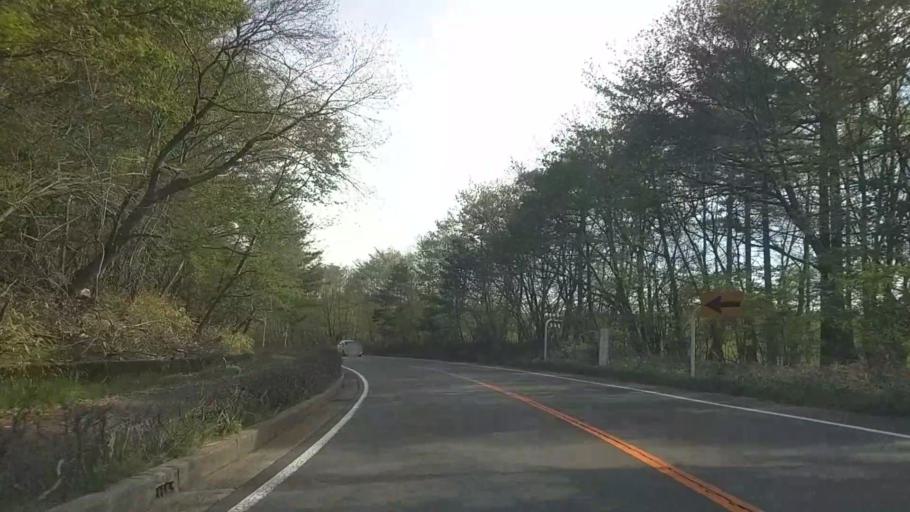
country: JP
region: Yamanashi
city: Nirasaki
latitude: 35.9321
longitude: 138.4472
